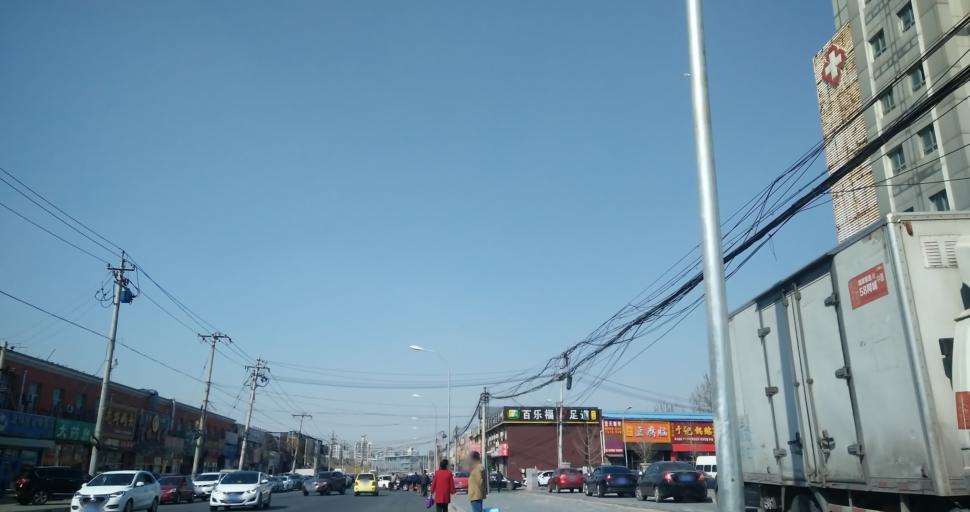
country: CN
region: Beijing
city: Jiugong
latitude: 39.8061
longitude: 116.4377
